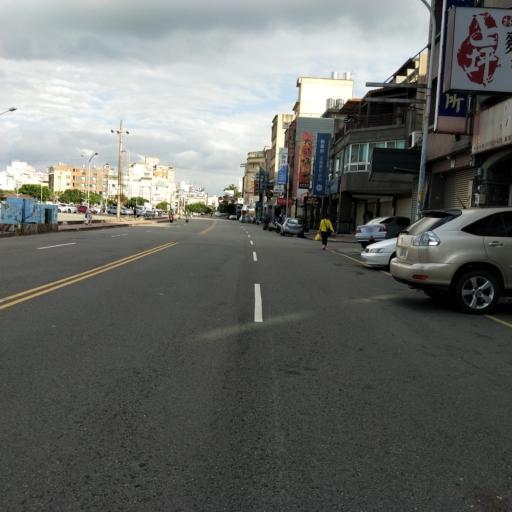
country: TW
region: Taiwan
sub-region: Hsinchu
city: Zhubei
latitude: 24.8330
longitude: 121.0072
